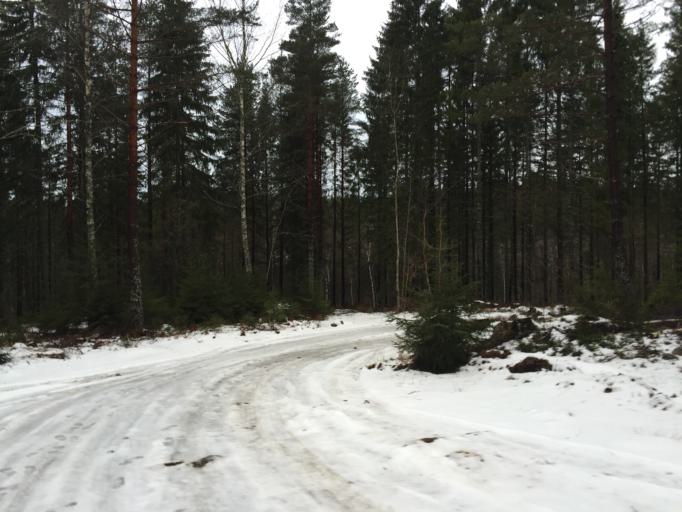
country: SE
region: Soedermanland
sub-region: Vingakers Kommun
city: Vingaker
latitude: 58.9972
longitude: 15.6827
